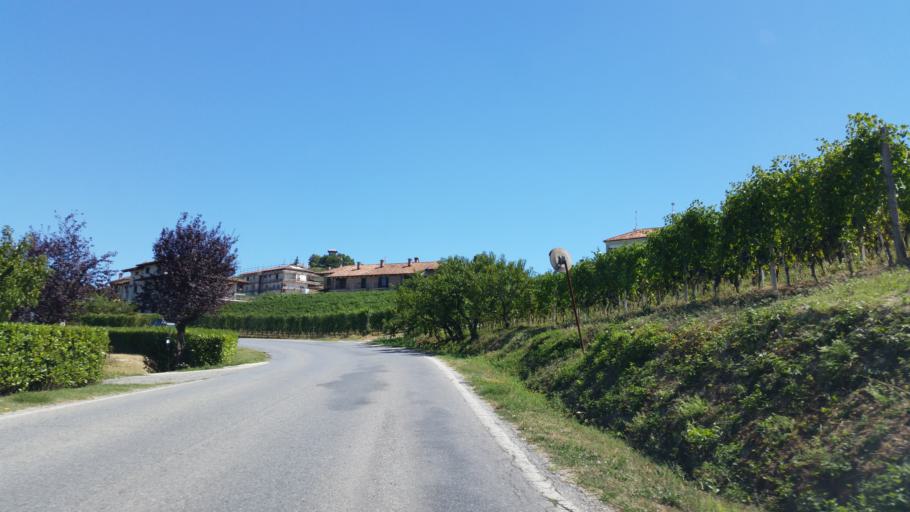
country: IT
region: Piedmont
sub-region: Provincia di Cuneo
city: Barbaresco
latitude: 44.7052
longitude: 8.0763
